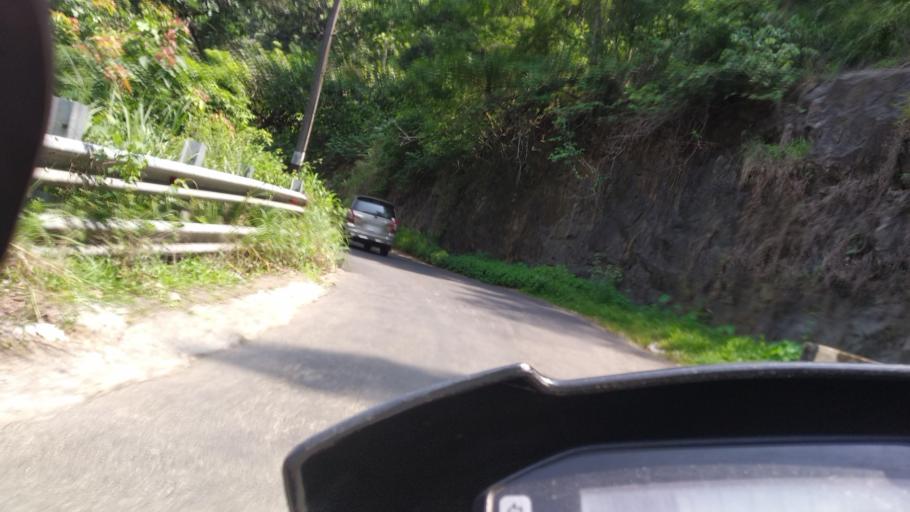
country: IN
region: Kerala
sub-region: Kottayam
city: Erattupetta
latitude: 9.6956
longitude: 76.8689
